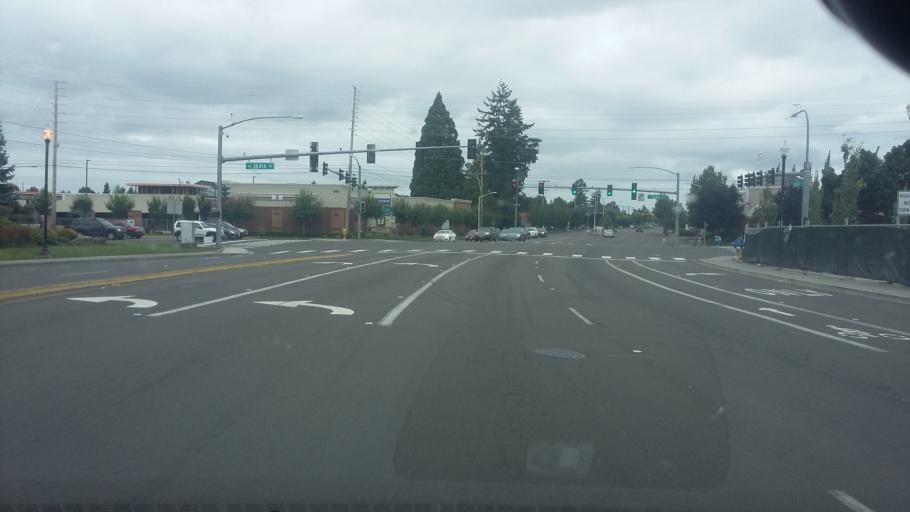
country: US
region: Washington
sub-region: Clark County
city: Mill Plain
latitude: 45.6155
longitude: -122.5032
